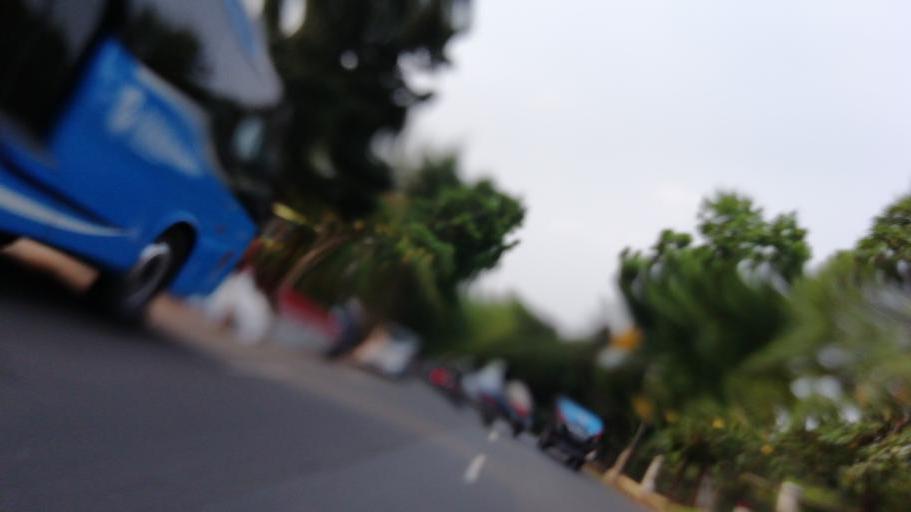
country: ID
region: West Java
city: Depok
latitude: -6.3535
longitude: 106.8319
